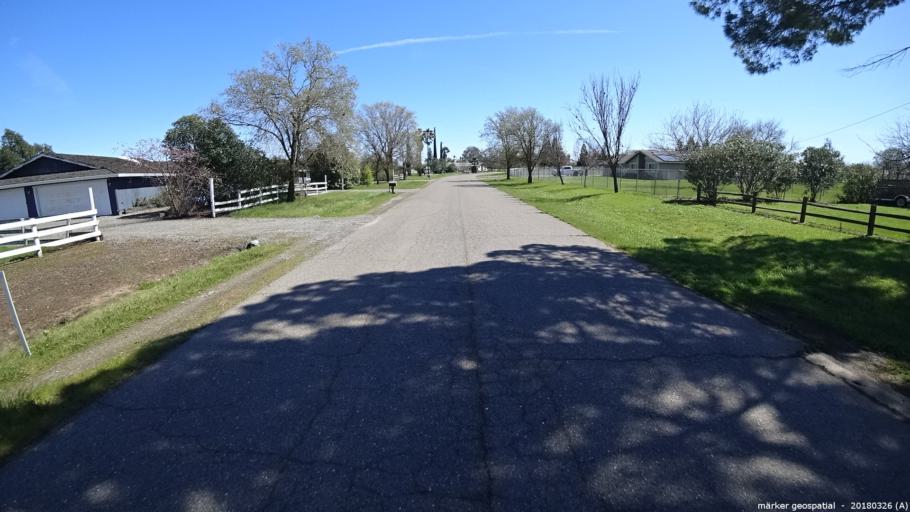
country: US
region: California
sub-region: Sacramento County
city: Wilton
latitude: 38.4831
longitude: -121.2351
